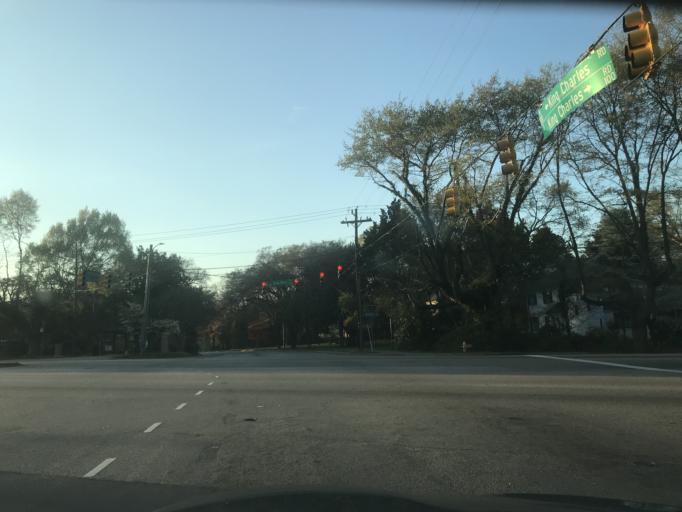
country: US
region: North Carolina
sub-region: Wake County
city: Raleigh
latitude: 35.7795
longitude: -78.6080
